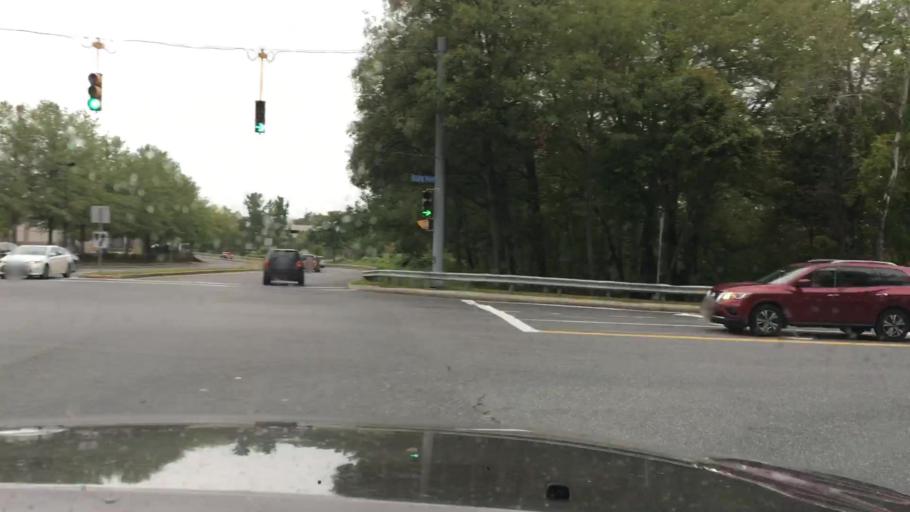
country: US
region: Massachusetts
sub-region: Middlesex County
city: Framingham
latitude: 42.3009
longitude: -71.3924
